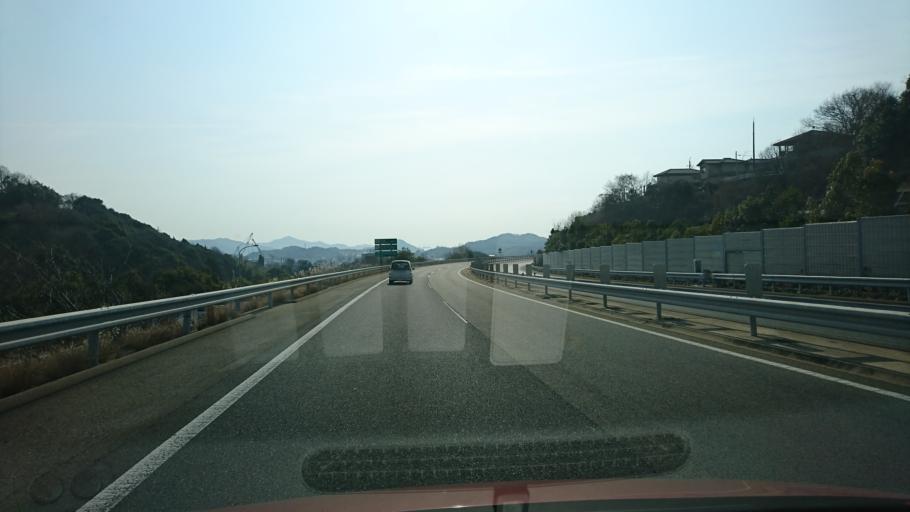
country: JP
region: Hiroshima
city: Onomichi
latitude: 34.4172
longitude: 133.2198
